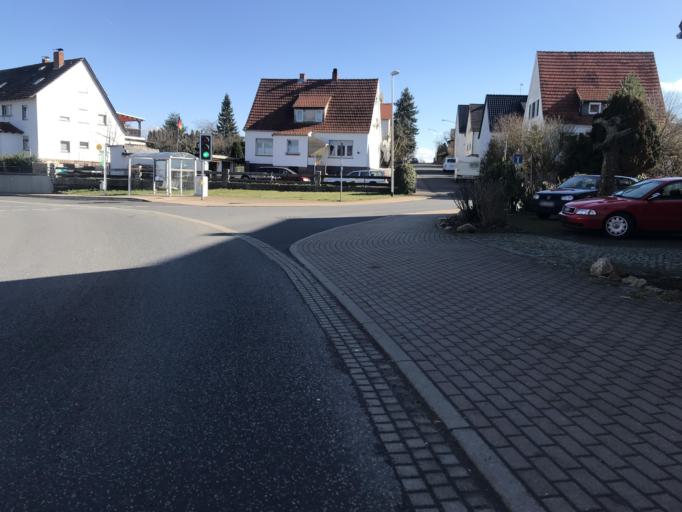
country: DE
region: Hesse
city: Schwalmstadt
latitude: 50.9042
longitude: 9.2178
